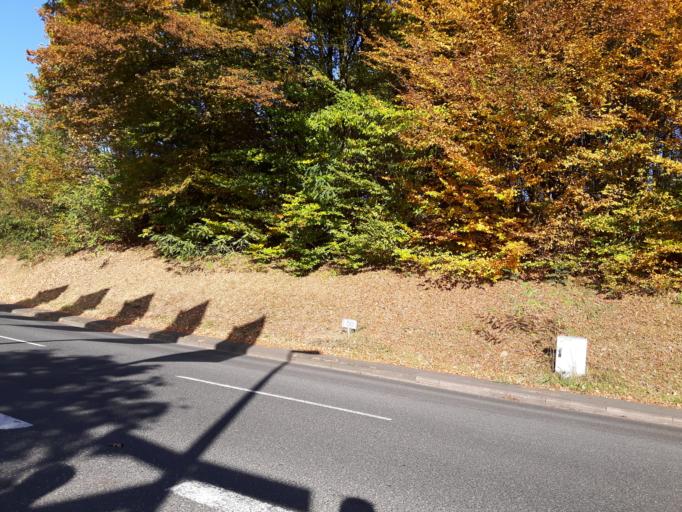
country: DE
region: Bavaria
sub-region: Regierungsbezirk Unterfranken
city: Mespelbrunn
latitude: 49.9038
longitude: 9.2984
